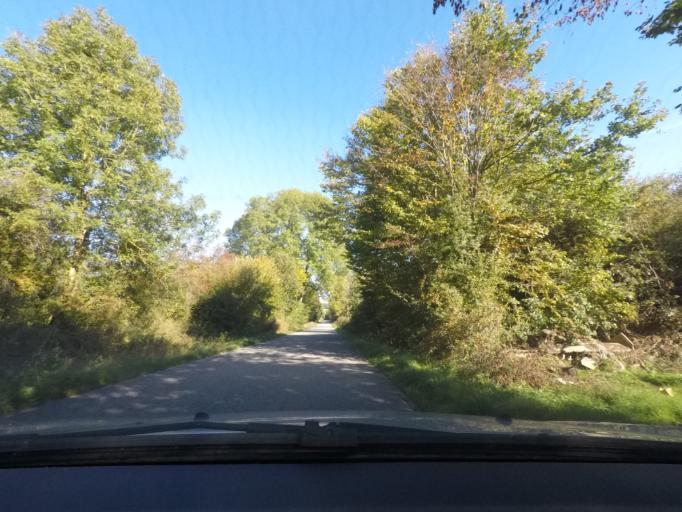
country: BE
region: Wallonia
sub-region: Province du Luxembourg
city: Etalle
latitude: 49.7107
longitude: 5.5657
